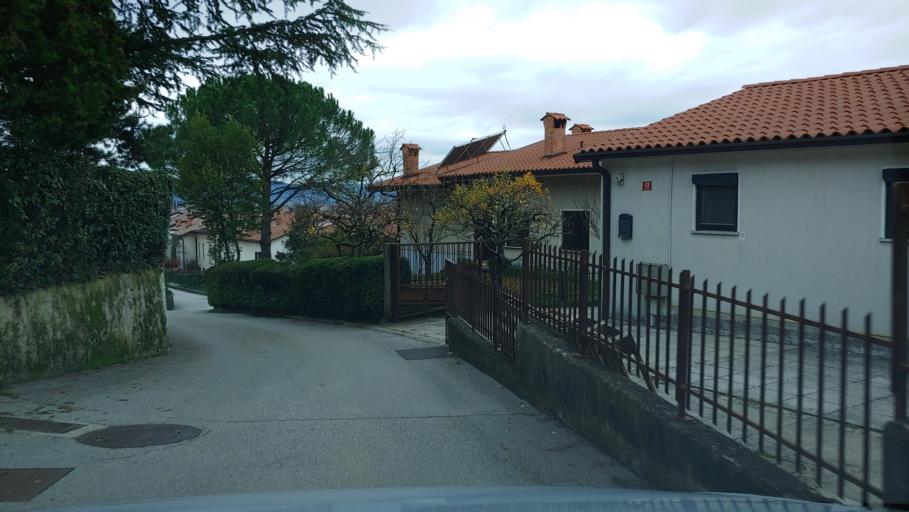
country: SI
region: Sempeter-Vrtojba
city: Sempeter pri Gorici
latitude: 45.9187
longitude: 13.6437
